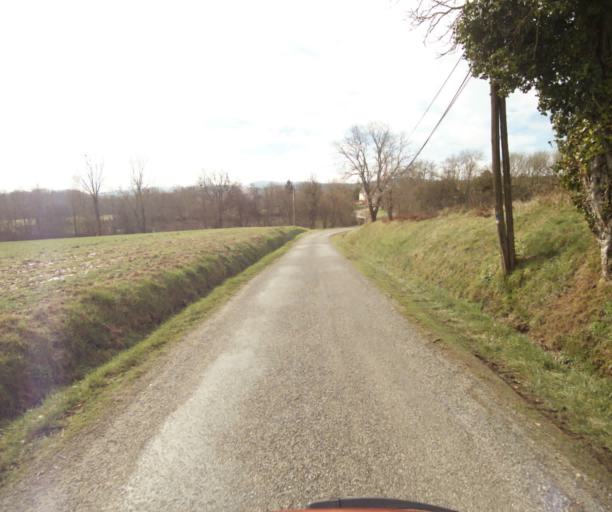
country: FR
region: Midi-Pyrenees
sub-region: Departement de l'Ariege
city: Pamiers
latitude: 43.1060
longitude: 1.5348
